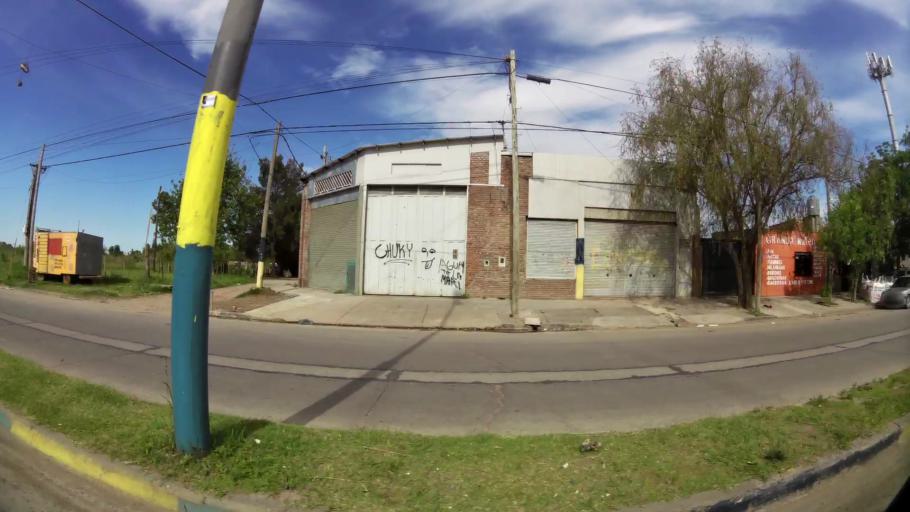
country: AR
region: Santa Fe
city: Granadero Baigorria
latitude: -32.9138
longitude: -60.7139
